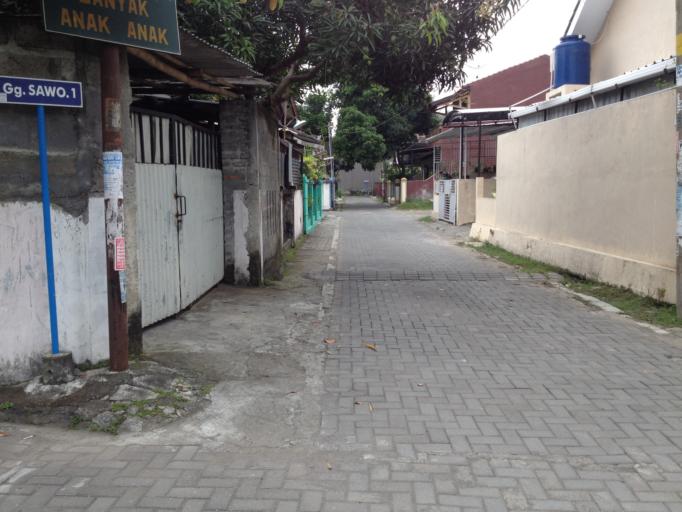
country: ID
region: Daerah Istimewa Yogyakarta
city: Yogyakarta
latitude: -7.8238
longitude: 110.3753
